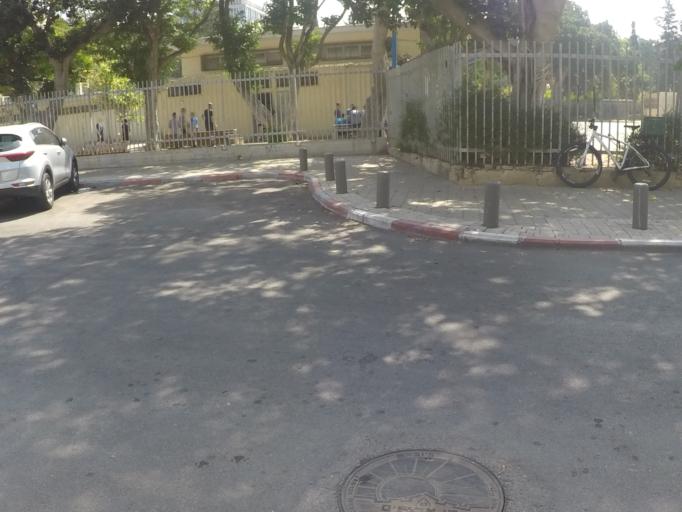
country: IL
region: Tel Aviv
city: Ramat Gan
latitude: 32.1100
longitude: 34.7949
